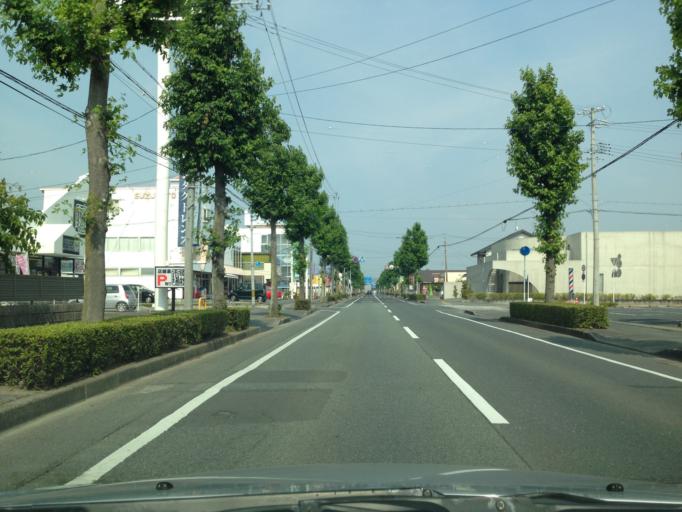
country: JP
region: Shizuoka
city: Hamakita
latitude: 34.8096
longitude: 137.7986
